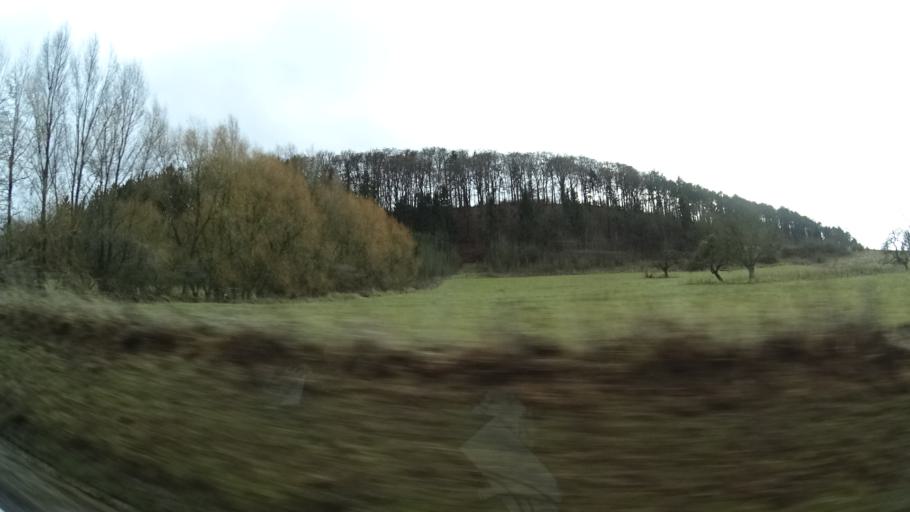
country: DE
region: Thuringia
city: Oberkatz
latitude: 50.6058
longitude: 10.2332
